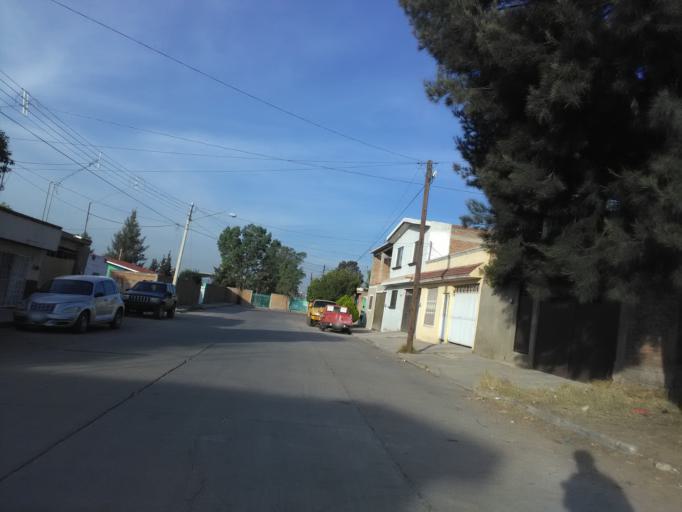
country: MX
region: Durango
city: Victoria de Durango
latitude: 24.0448
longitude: -104.6484
